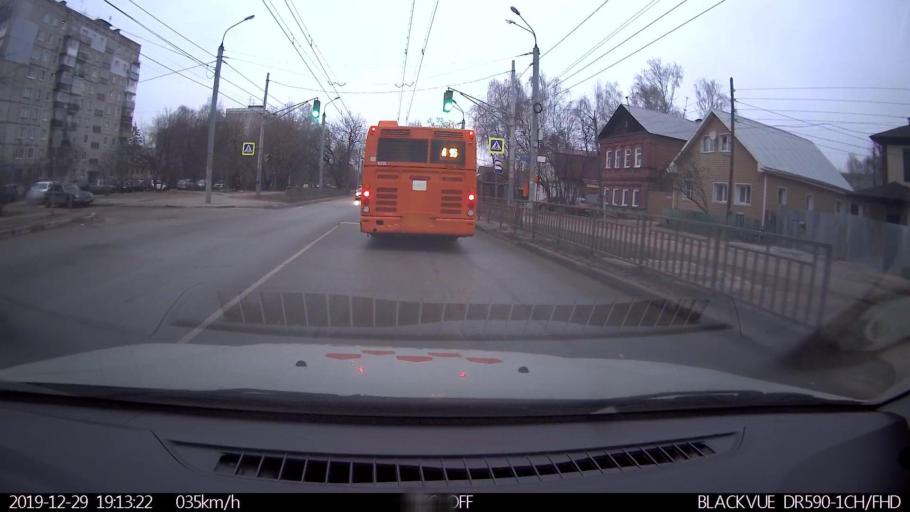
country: RU
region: Nizjnij Novgorod
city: Neklyudovo
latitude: 56.3626
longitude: 43.8578
